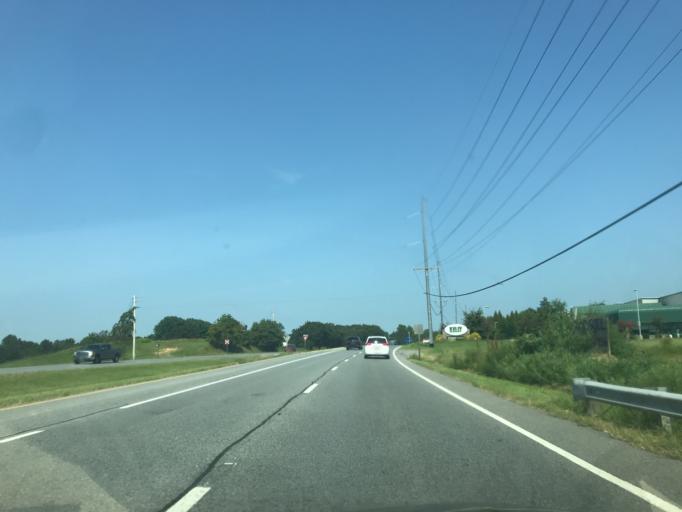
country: US
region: Maryland
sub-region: Calvert County
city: Dunkirk Town Center
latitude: 38.6838
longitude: -76.6344
